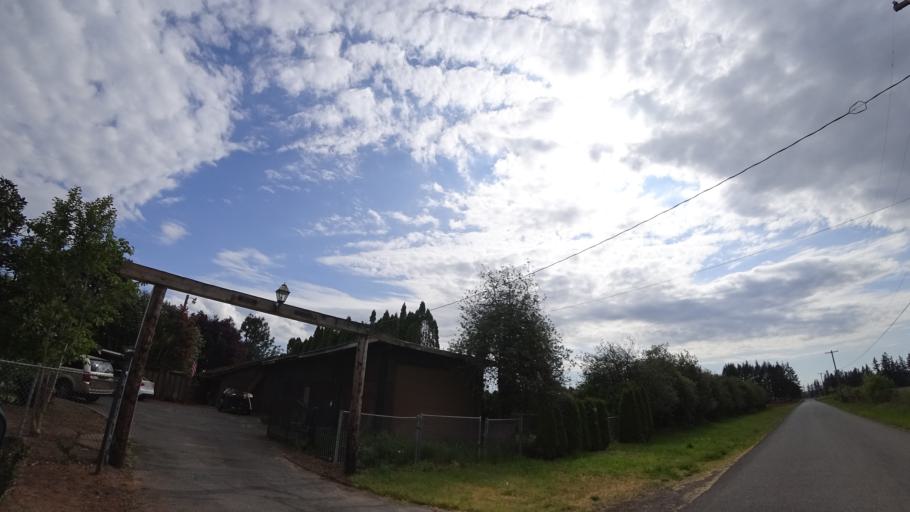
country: US
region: Oregon
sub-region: Washington County
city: Hillsboro
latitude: 45.4744
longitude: -122.9504
